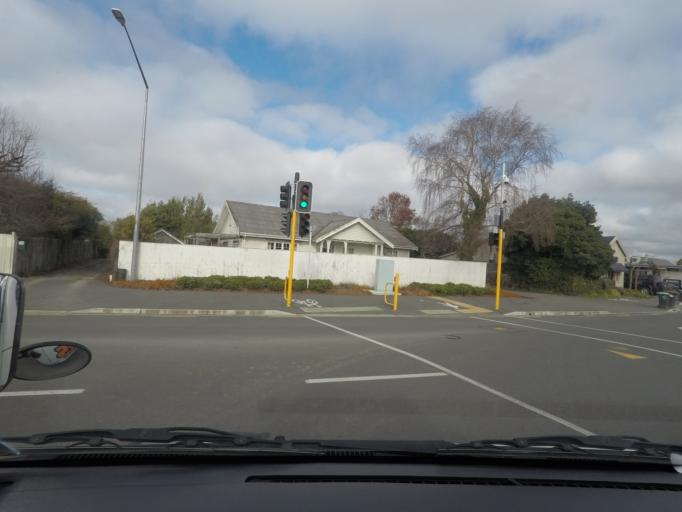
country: NZ
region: Canterbury
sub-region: Christchurch City
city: Christchurch
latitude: -43.5089
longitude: 172.6310
